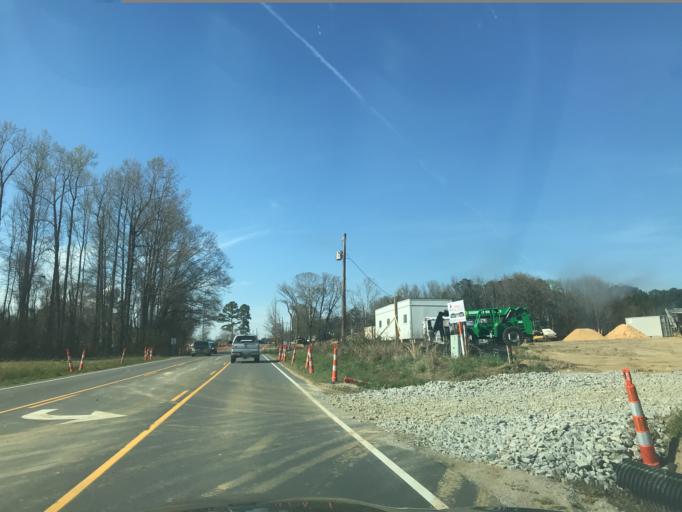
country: US
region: North Carolina
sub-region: Harnett County
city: Angier
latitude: 35.5335
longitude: -78.7456
